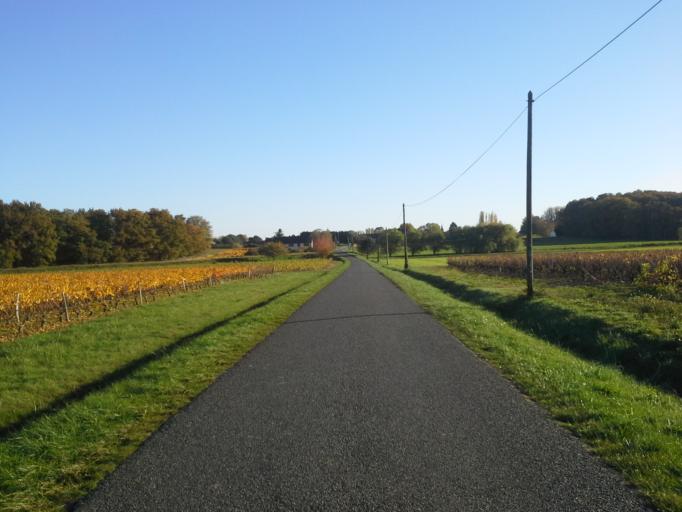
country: FR
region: Centre
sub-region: Departement du Loir-et-Cher
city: Saint-Romain-sur-Cher
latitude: 47.3688
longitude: 1.4004
